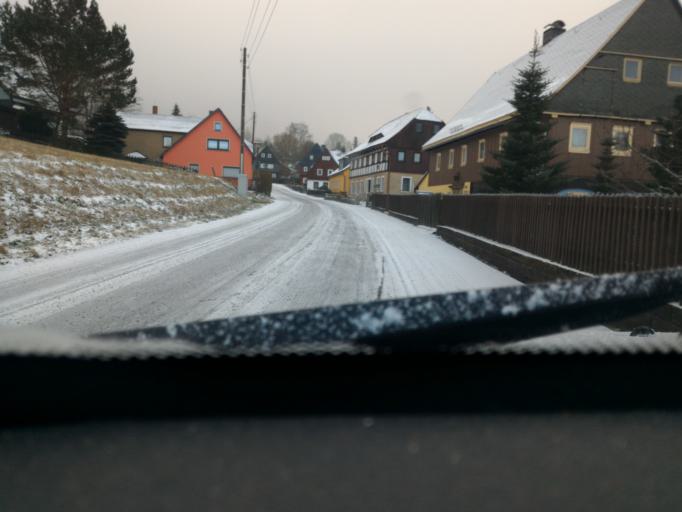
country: DE
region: Saxony
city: Grossschonau
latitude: 50.8604
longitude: 14.6528
